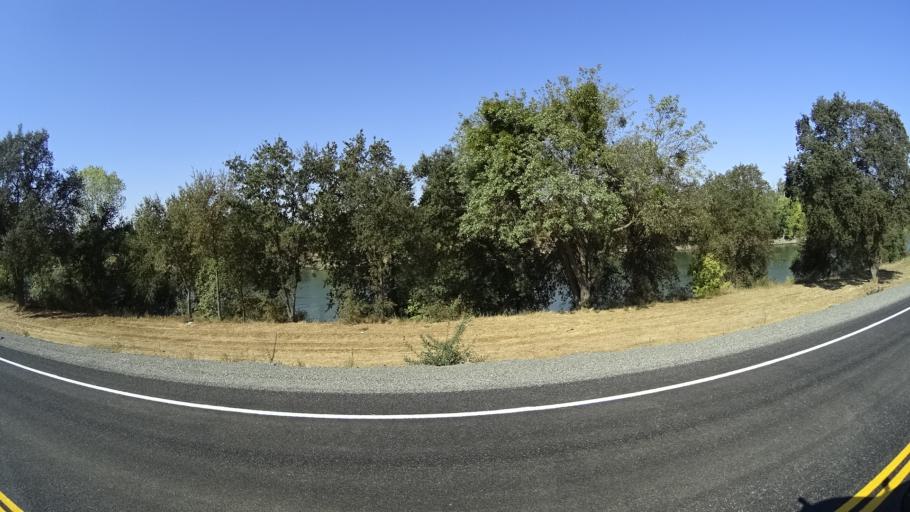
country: US
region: California
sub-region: Yolo County
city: West Sacramento
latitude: 38.6440
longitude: -121.5825
